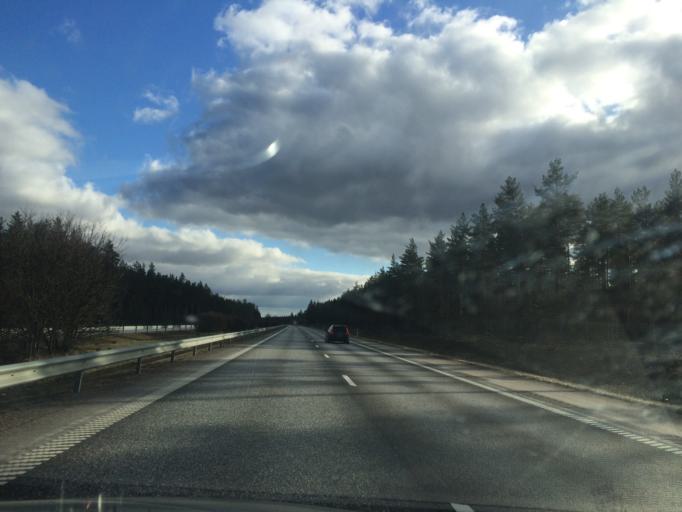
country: SE
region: Joenkoeping
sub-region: Vaggeryds Kommun
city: Skillingaryd
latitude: 57.3901
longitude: 14.0995
